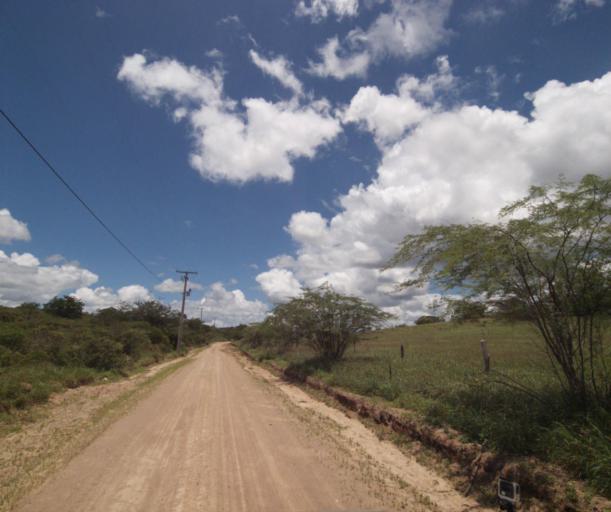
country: BR
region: Bahia
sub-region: Pocoes
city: Pocoes
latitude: -14.3824
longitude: -40.3837
